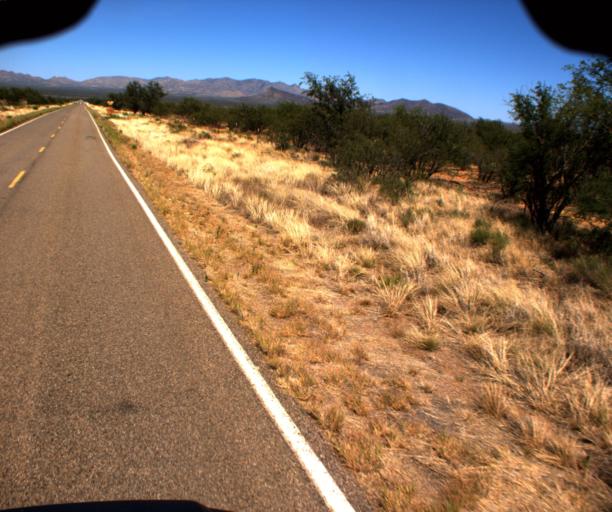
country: US
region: Arizona
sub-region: Pima County
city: Three Points
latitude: 31.8245
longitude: -111.4323
